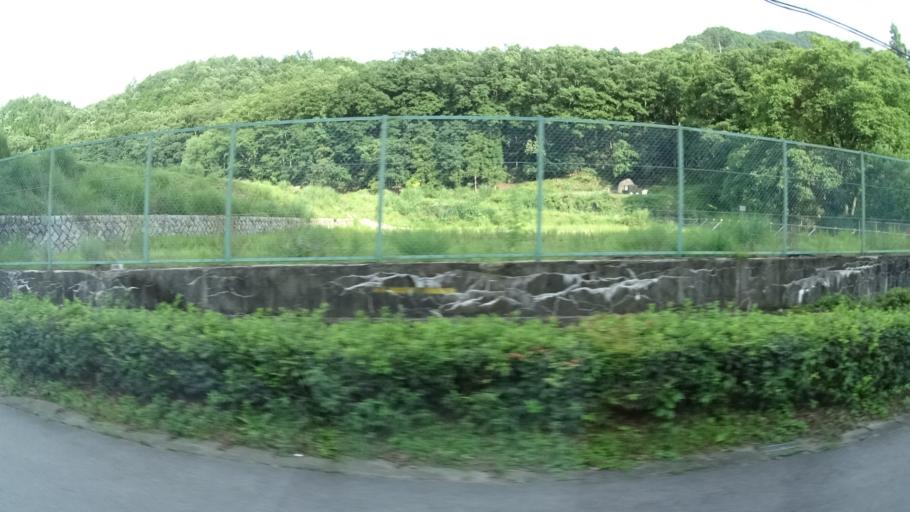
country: JP
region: Tochigi
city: Nikko
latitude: 36.6537
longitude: 139.4542
